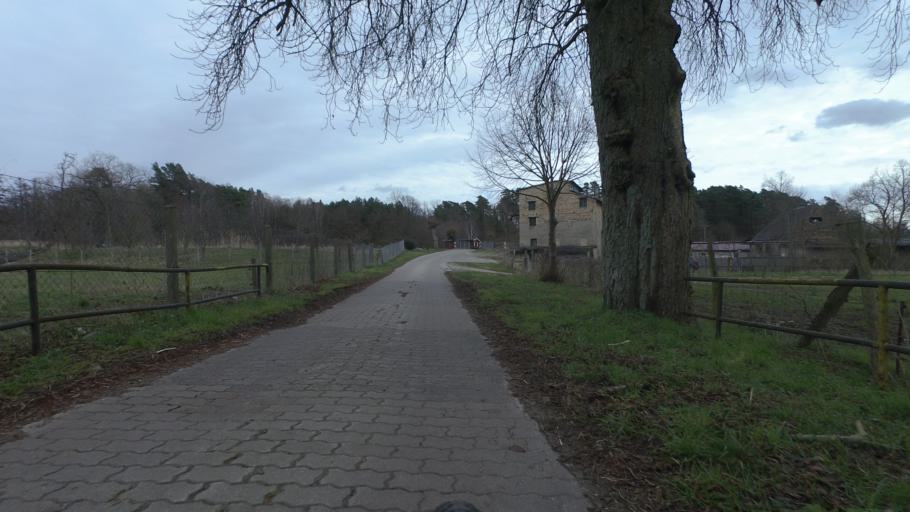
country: DE
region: Brandenburg
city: Lindow
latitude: 52.9948
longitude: 12.9545
